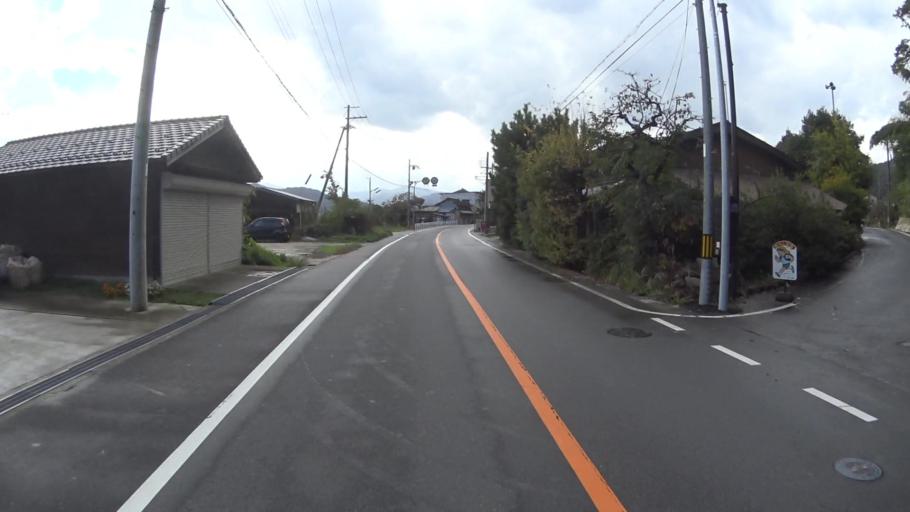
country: JP
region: Kyoto
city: Miyazu
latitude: 35.5470
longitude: 135.1336
